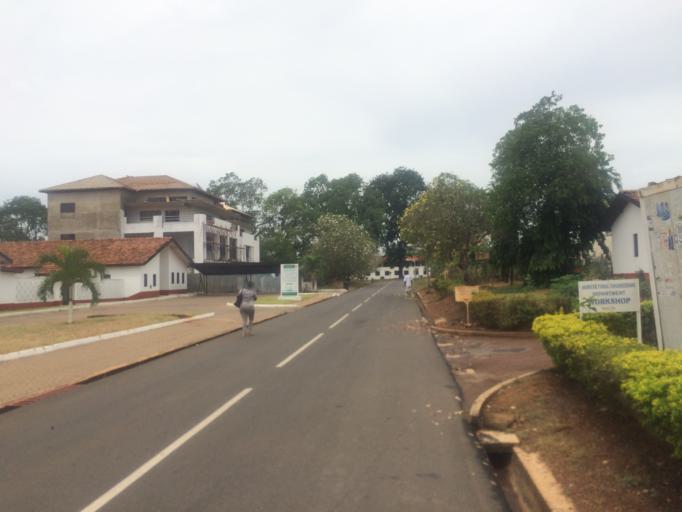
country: GH
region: Greater Accra
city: Medina Estates
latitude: 5.6494
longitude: -0.1836
